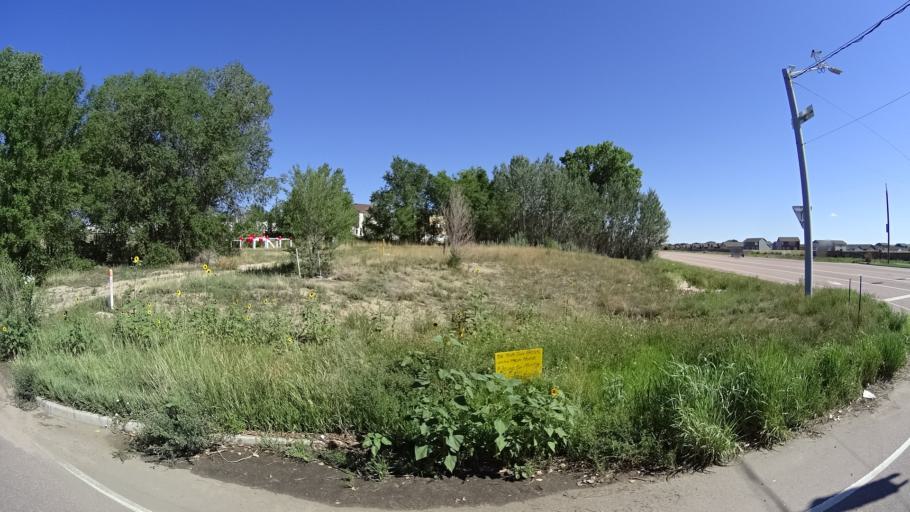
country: US
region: Colorado
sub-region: El Paso County
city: Security-Widefield
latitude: 38.7375
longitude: -104.6500
